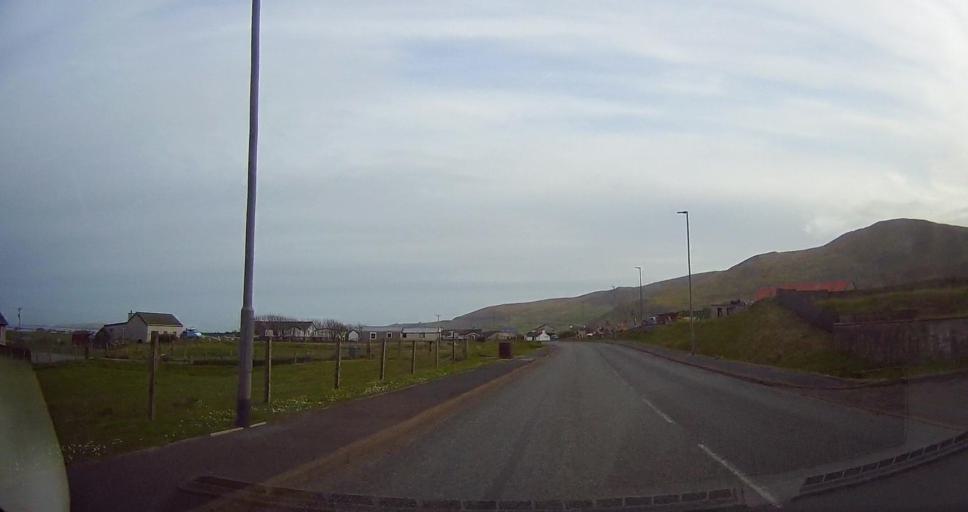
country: GB
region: Scotland
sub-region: Shetland Islands
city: Sandwick
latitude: 60.0423
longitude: -1.2295
